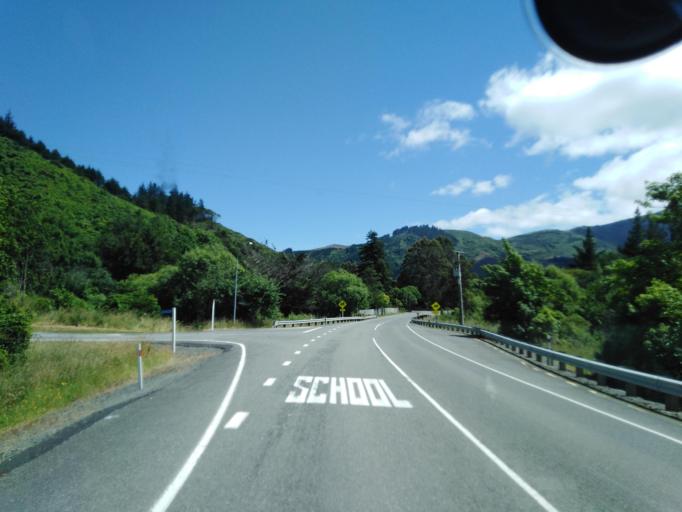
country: NZ
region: Nelson
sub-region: Nelson City
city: Nelson
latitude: -41.2179
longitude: 173.3962
